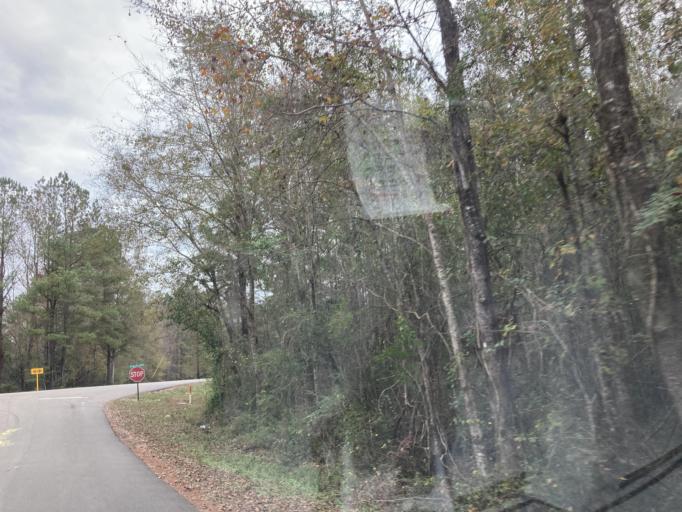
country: US
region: Mississippi
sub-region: Perry County
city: New Augusta
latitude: 31.0652
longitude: -89.1914
